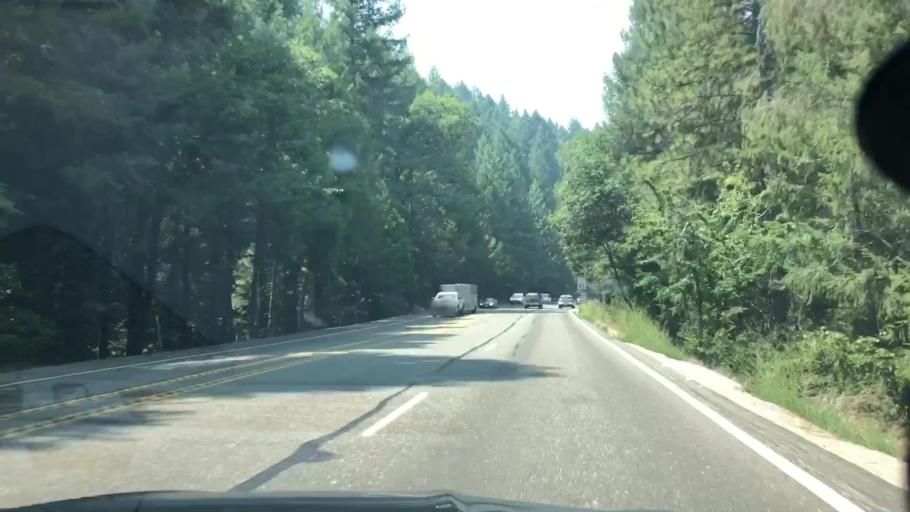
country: US
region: California
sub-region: El Dorado County
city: Pollock Pines
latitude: 38.7635
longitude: -120.5482
